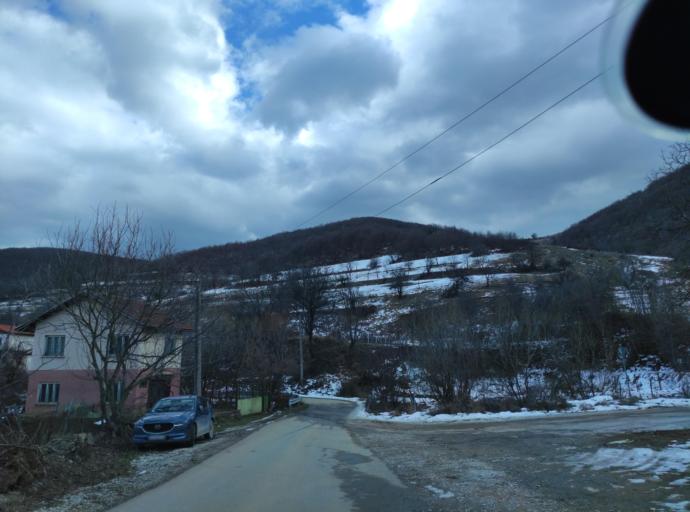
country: BG
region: Montana
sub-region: Obshtina Chiprovtsi
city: Chiprovtsi
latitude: 43.3773
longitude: 22.8730
